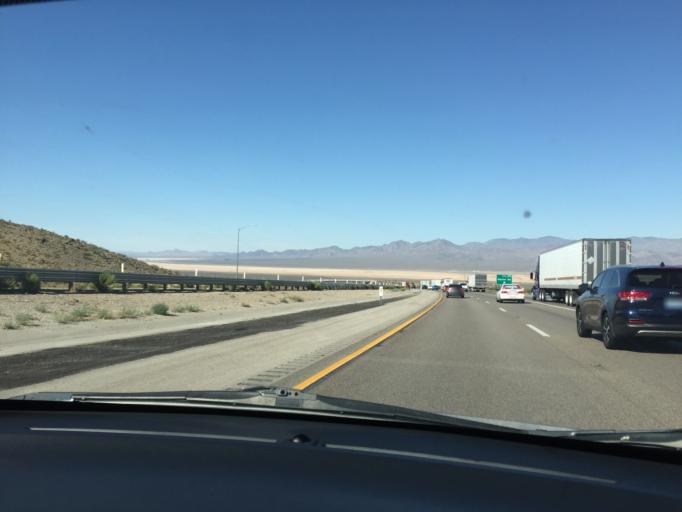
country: US
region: Nevada
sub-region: Clark County
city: Sandy Valley
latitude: 35.4688
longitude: -115.4534
